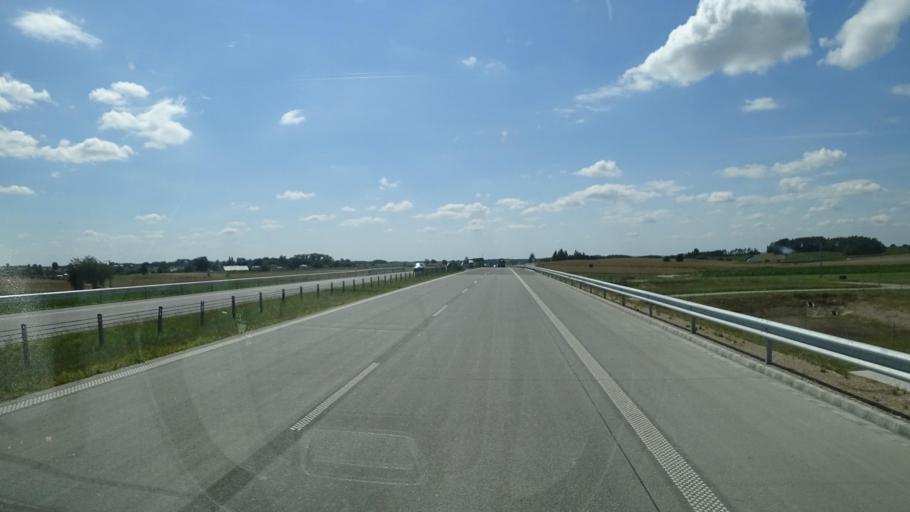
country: PL
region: Podlasie
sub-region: Powiat lomzynski
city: Piatnica
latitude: 53.2618
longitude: 22.1175
